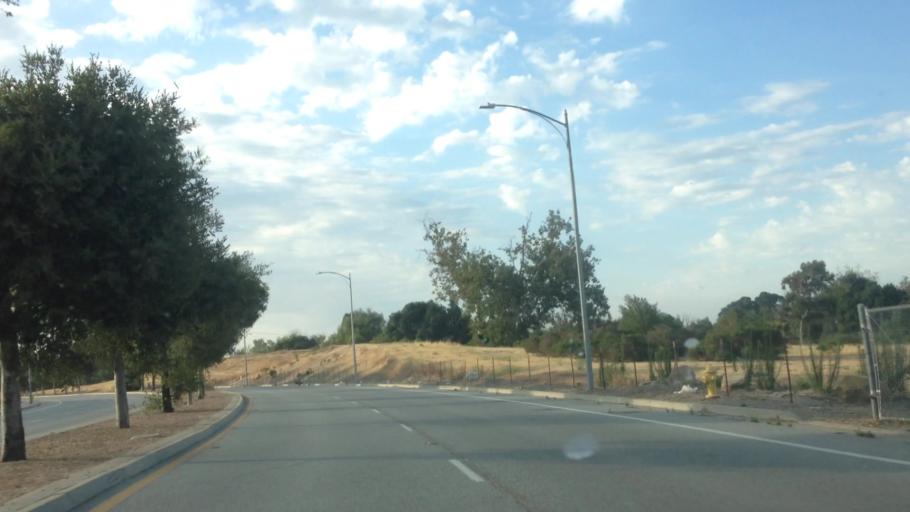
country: US
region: California
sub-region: Santa Clara County
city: Seven Trees
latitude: 37.2539
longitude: -121.7766
